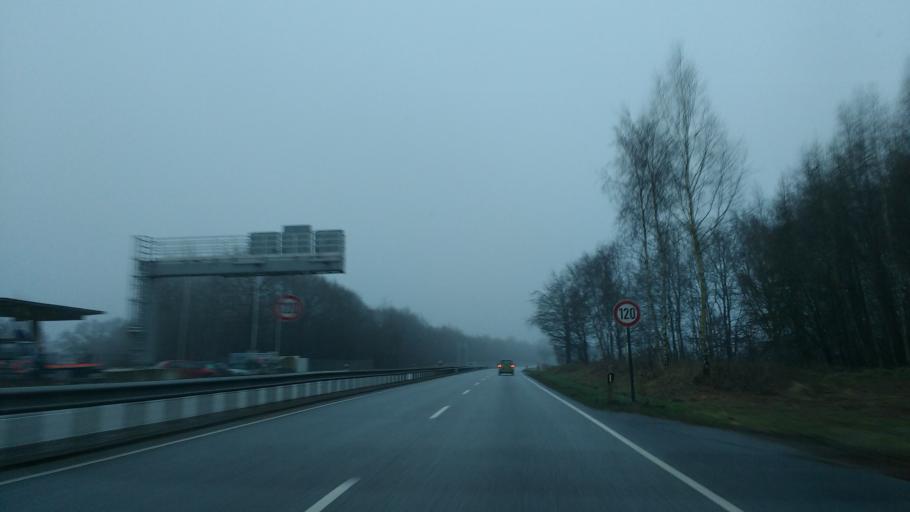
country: DE
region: Schleswig-Holstein
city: Westerronfeld
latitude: 54.2745
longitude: 9.6640
